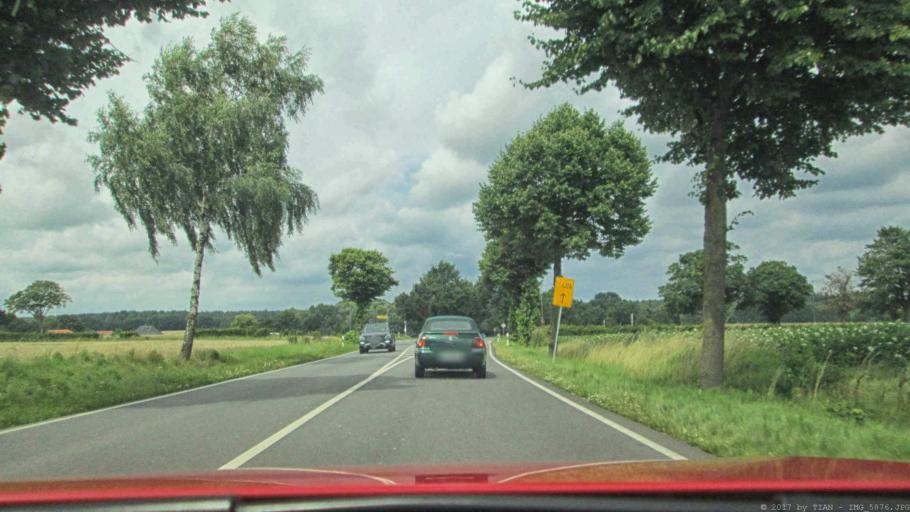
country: DE
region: Lower Saxony
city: Bad Bevensen
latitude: 53.0740
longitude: 10.5627
